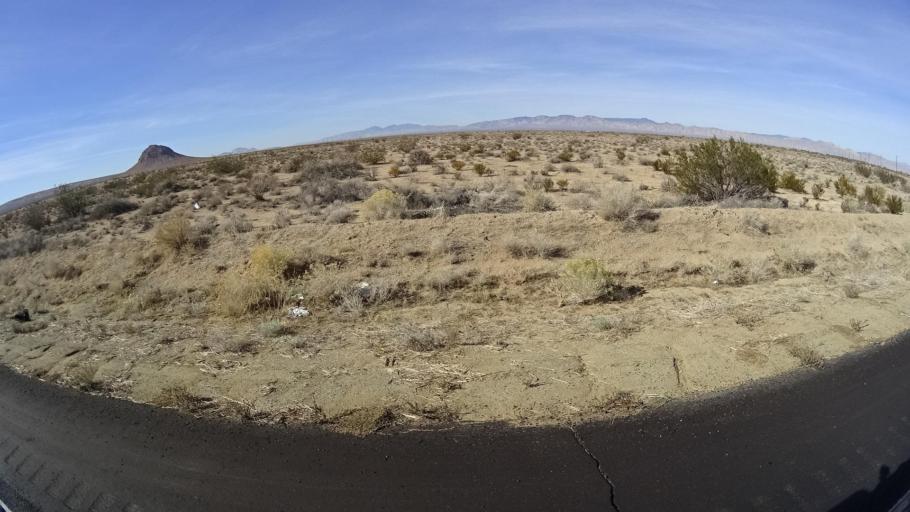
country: US
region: California
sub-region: Kern County
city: California City
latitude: 35.1008
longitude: -117.9174
